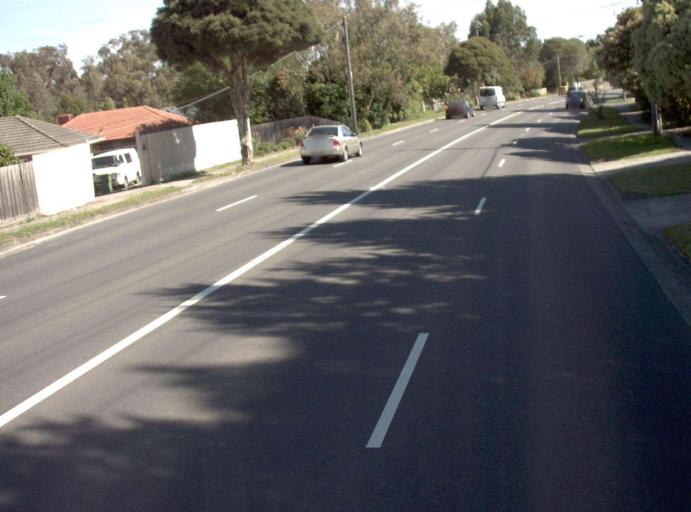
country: AU
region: Victoria
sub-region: Knox
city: Bayswater
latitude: -37.8631
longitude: 145.2657
